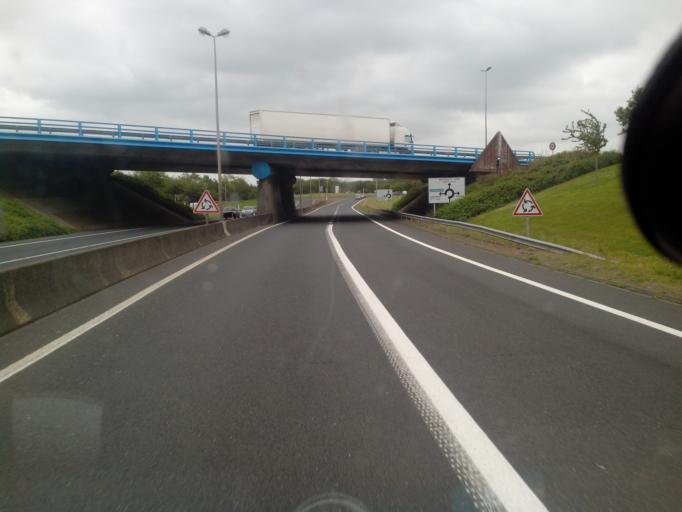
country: FR
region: Lower Normandy
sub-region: Departement du Calvados
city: Bretteville-sur-Odon
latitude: 49.1647
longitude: -0.4291
